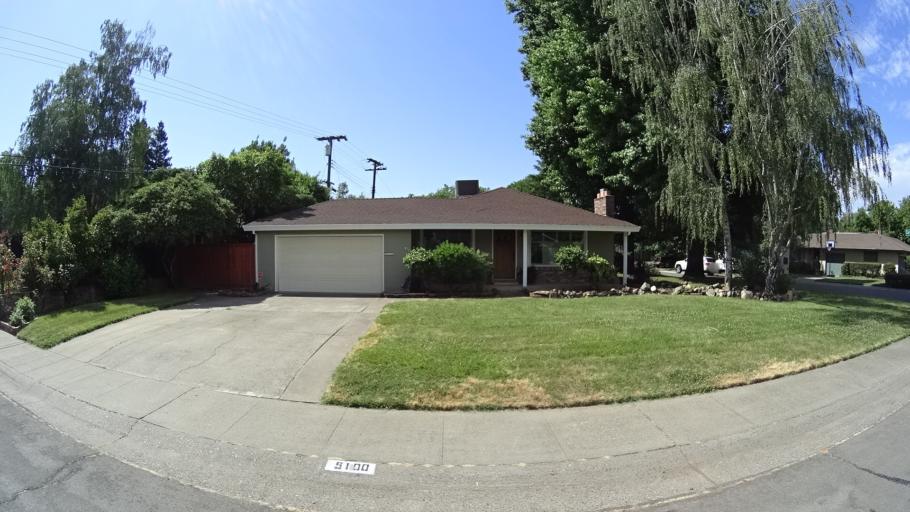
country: US
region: California
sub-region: Sacramento County
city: Sacramento
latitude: 38.5804
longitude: -121.4360
